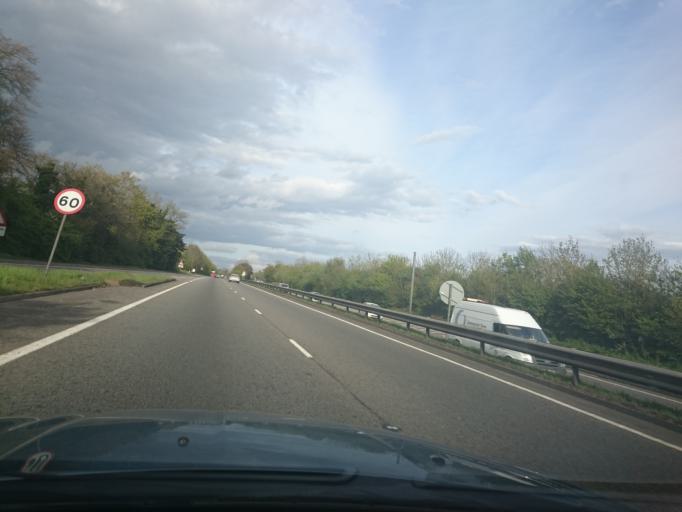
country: GB
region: England
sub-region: Surrey
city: Seale
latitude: 51.2262
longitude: -0.7206
